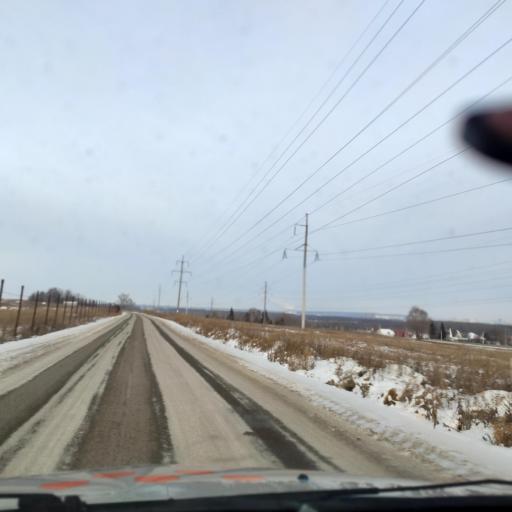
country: RU
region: Bashkortostan
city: Avdon
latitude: 54.7488
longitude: 55.7941
